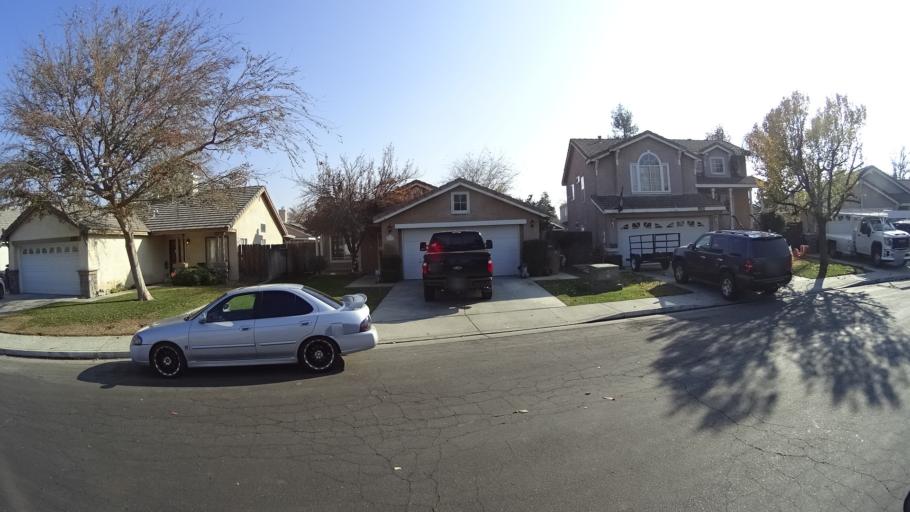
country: US
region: California
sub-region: Kern County
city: Greenacres
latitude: 35.3219
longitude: -119.0954
